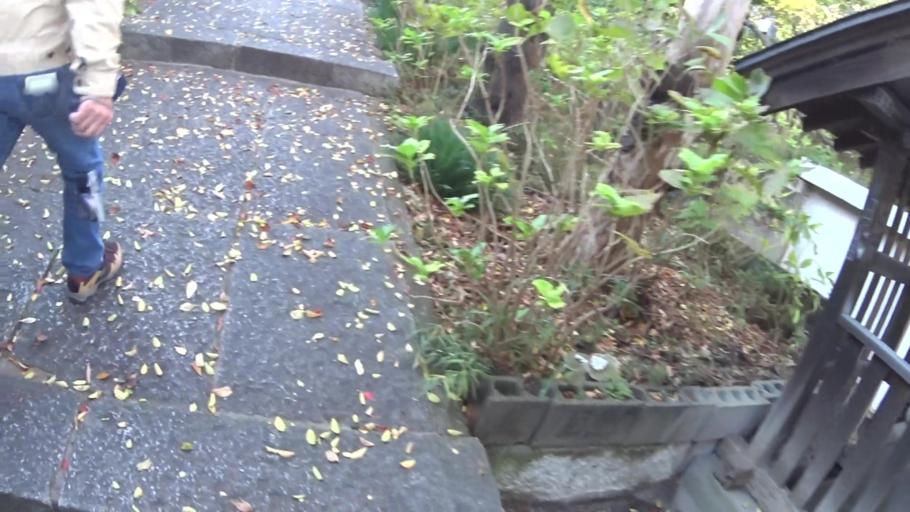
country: JP
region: Tokyo
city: Chofugaoka
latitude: 35.6322
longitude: 139.5148
